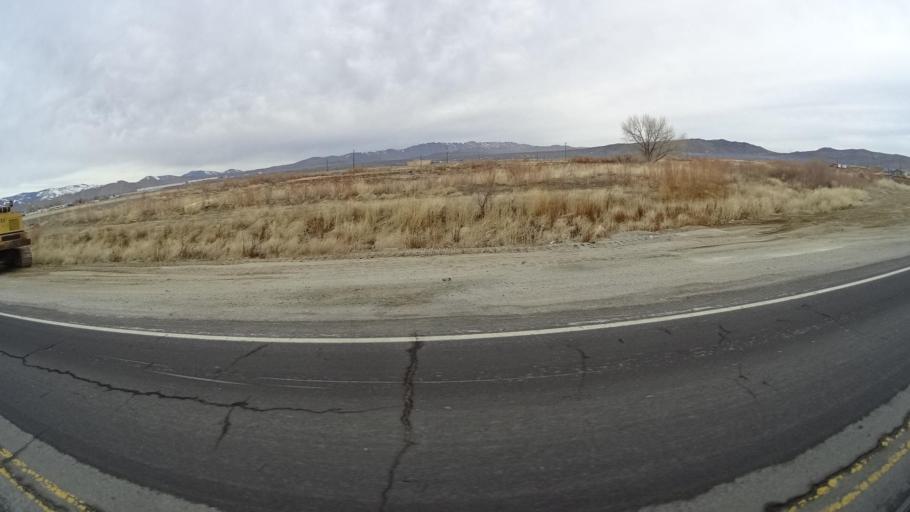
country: US
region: Nevada
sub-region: Washoe County
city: Lemmon Valley
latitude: 39.6469
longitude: -119.8304
